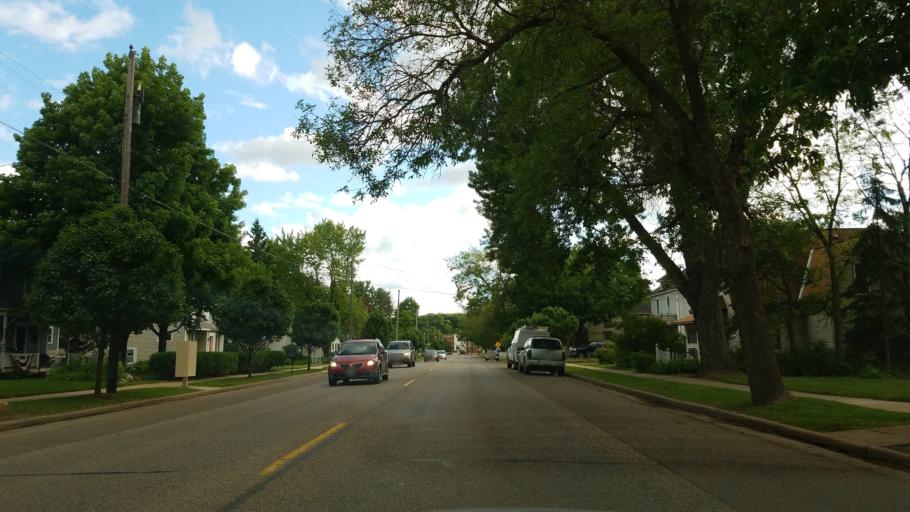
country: US
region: Wisconsin
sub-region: Polk County
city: Osceola
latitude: 45.3253
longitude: -92.7017
